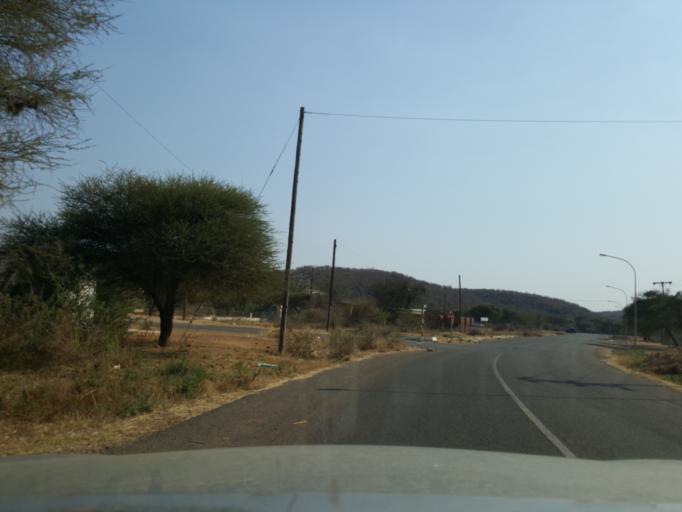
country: BW
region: South East
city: Lobatse
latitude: -25.1869
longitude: 25.6943
